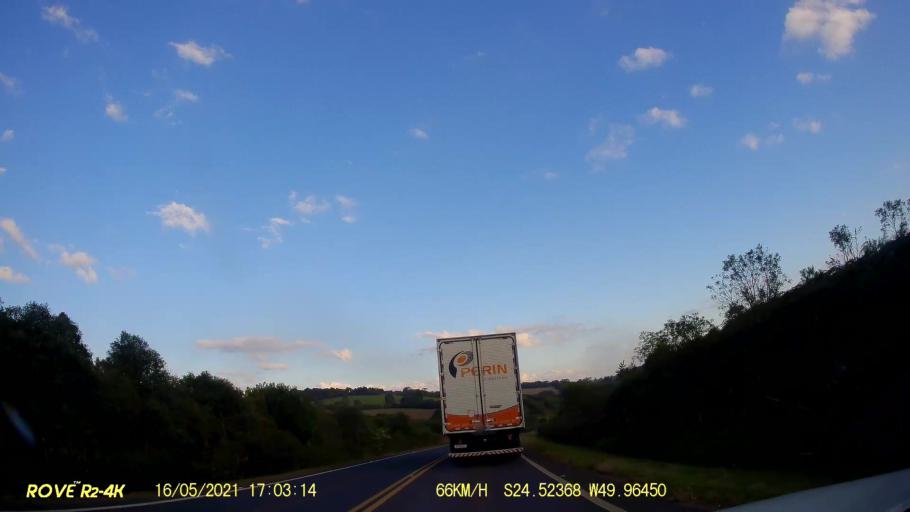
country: BR
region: Parana
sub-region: Pirai Do Sul
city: Pirai do Sul
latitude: -24.5233
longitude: -49.9649
